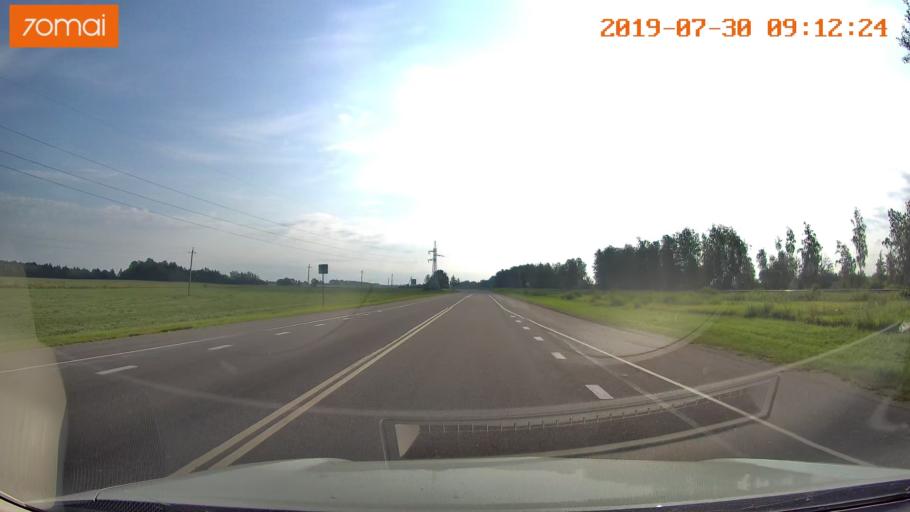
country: RU
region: Kaliningrad
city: Nesterov
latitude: 54.6165
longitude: 22.4736
